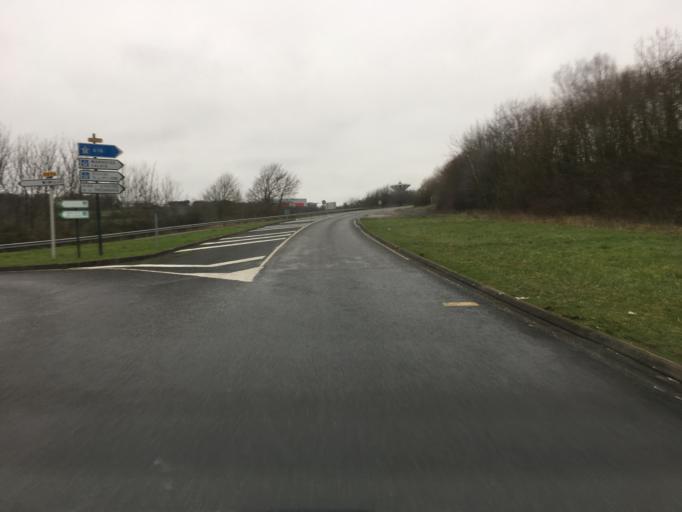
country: FR
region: Nord-Pas-de-Calais
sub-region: Departement du Pas-de-Calais
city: Wimille
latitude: 50.7653
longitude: 1.6380
